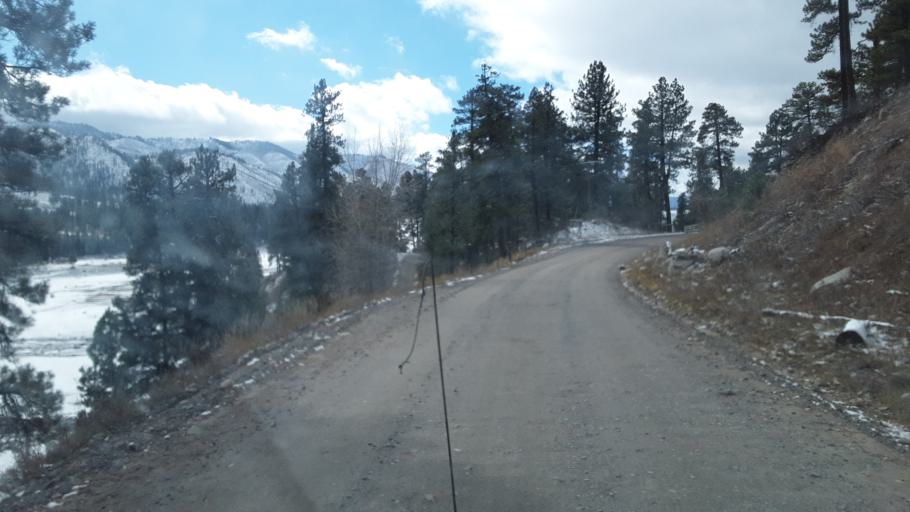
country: US
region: Colorado
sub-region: La Plata County
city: Bayfield
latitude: 37.4075
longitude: -107.5330
